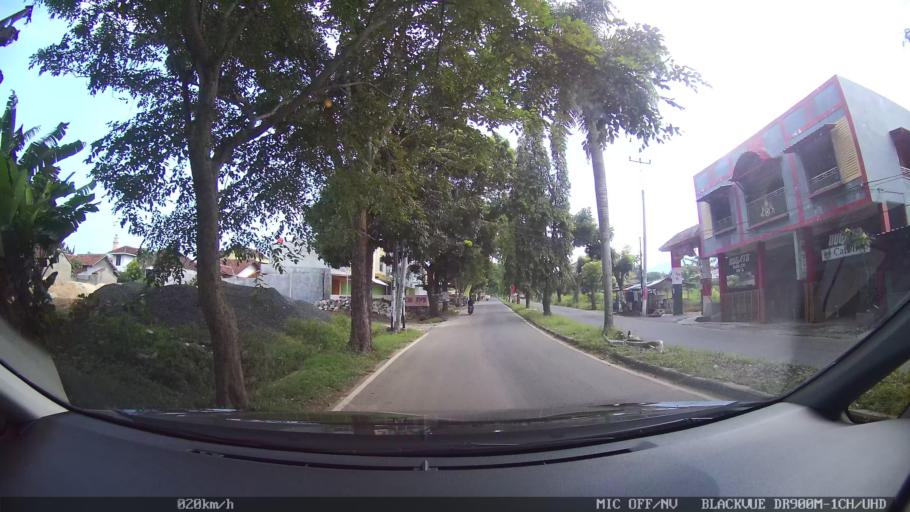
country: ID
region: Lampung
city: Kedaton
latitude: -5.3859
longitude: 105.2106
